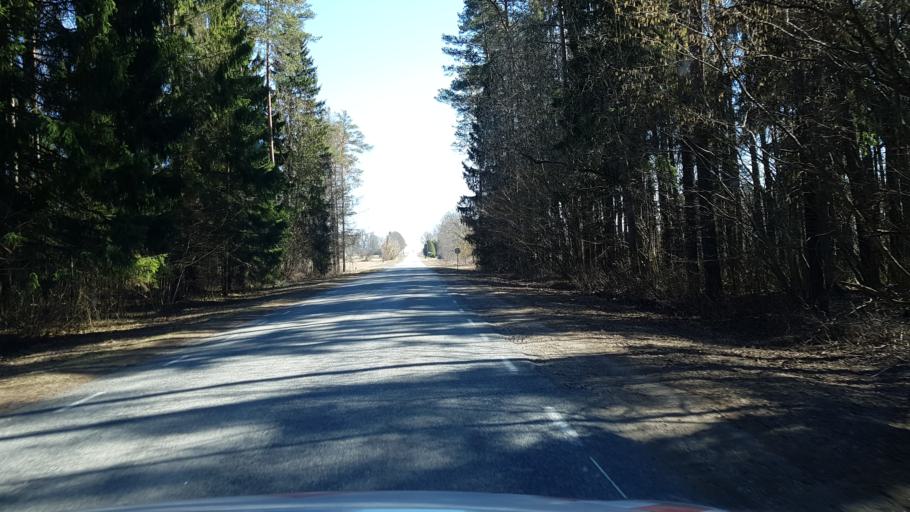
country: EE
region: Laeaene-Virumaa
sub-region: Vaeike-Maarja vald
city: Vaike-Maarja
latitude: 59.1184
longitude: 26.3229
